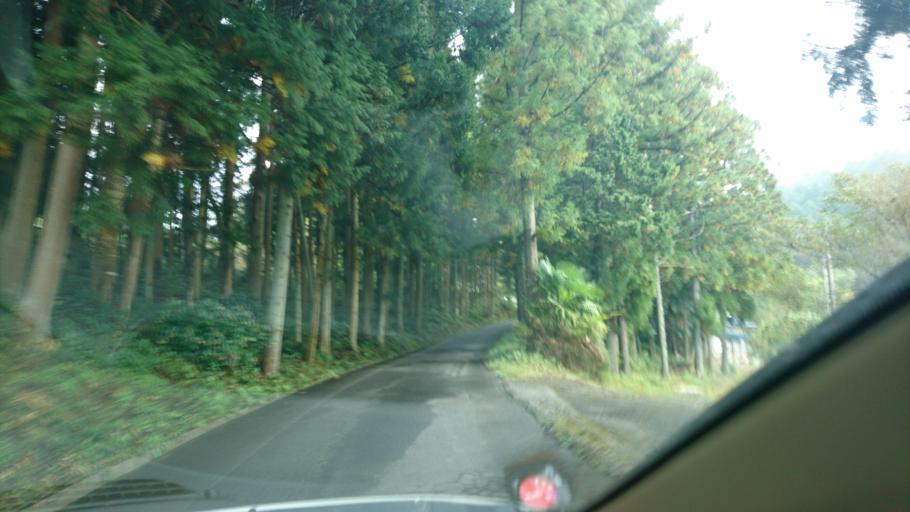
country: JP
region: Iwate
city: Ichinoseki
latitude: 38.9605
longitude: 141.1809
